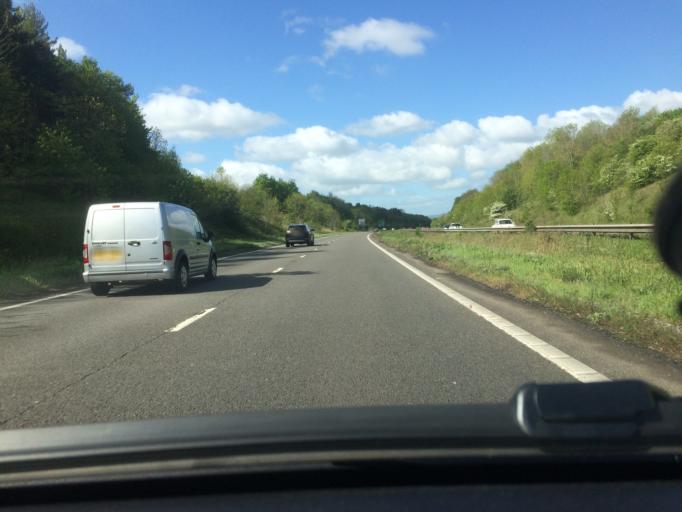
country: GB
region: England
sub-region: Cheshire West and Chester
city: Eccleston
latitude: 53.1596
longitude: -2.8870
